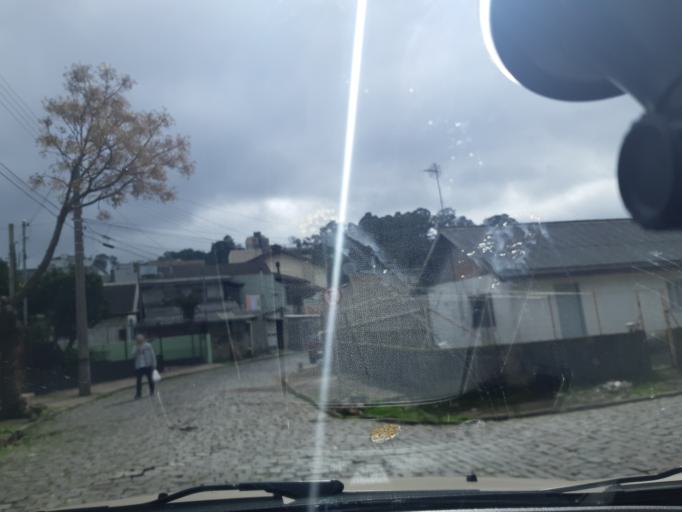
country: BR
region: Rio Grande do Sul
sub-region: Caxias Do Sul
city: Caxias do Sul
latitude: -29.1547
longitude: -51.2094
